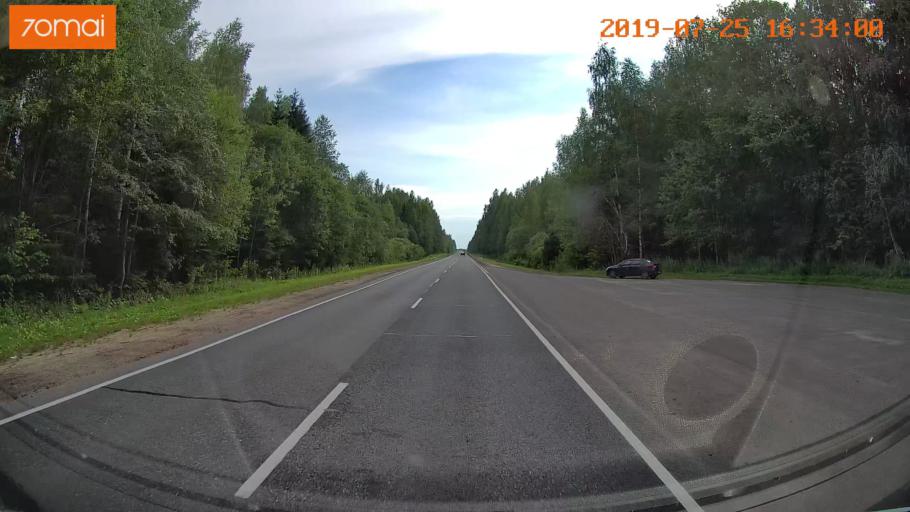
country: RU
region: Ivanovo
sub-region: Privolzhskiy Rayon
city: Ples
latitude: 57.4213
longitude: 41.4457
